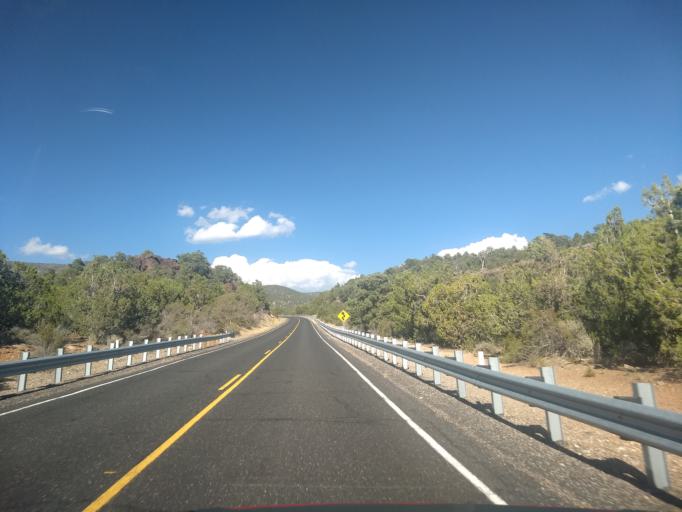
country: US
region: Utah
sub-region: Washington County
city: Enterprise
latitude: 37.4195
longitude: -113.5943
